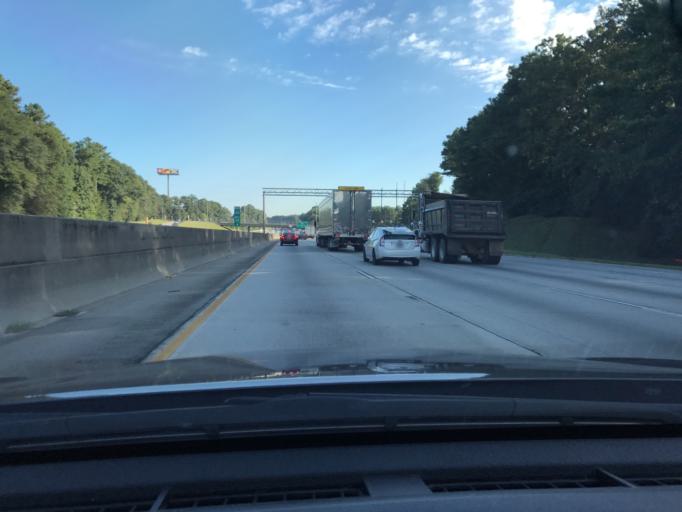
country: US
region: Georgia
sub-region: DeKalb County
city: Candler-McAfee
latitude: 33.7337
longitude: -84.2310
